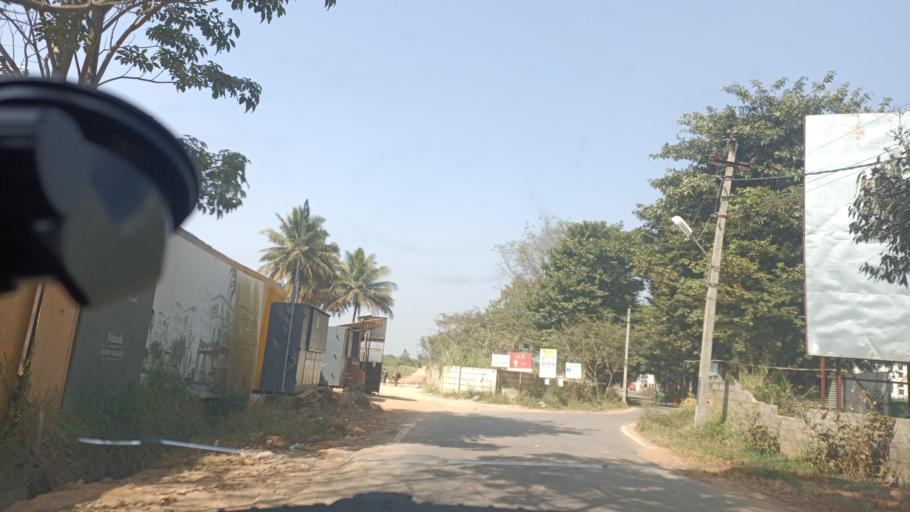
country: IN
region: Karnataka
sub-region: Bangalore Urban
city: Yelahanka
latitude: 13.1222
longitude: 77.6026
